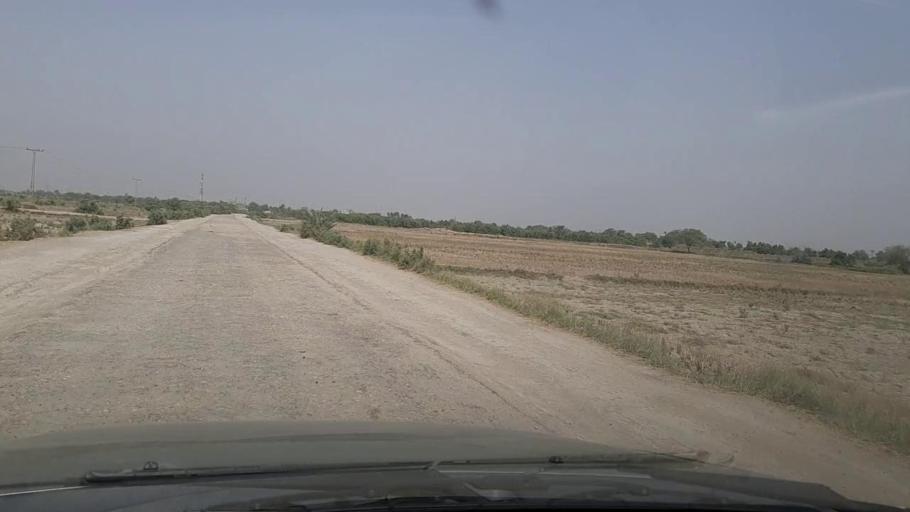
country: PK
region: Balochistan
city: Sohbatpur
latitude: 28.4209
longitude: 68.6800
